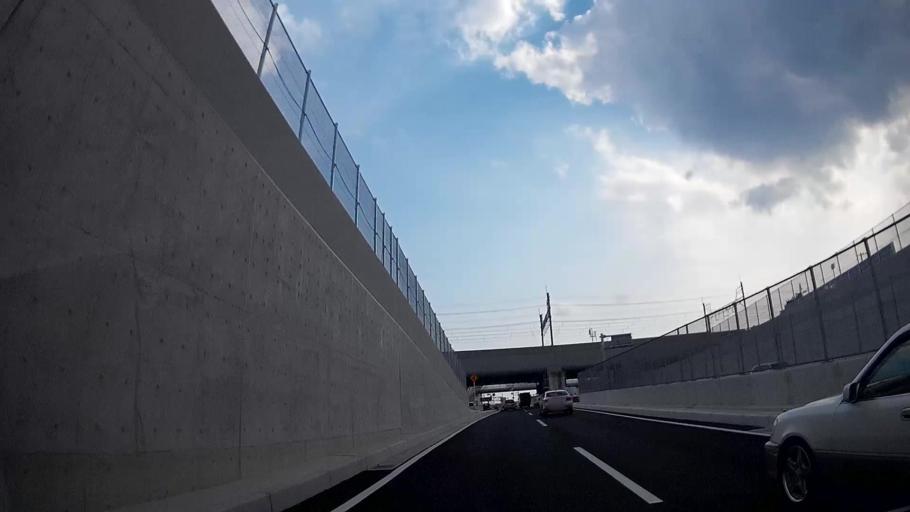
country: JP
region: Chiba
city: Matsudo
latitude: 35.7259
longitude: 139.9181
